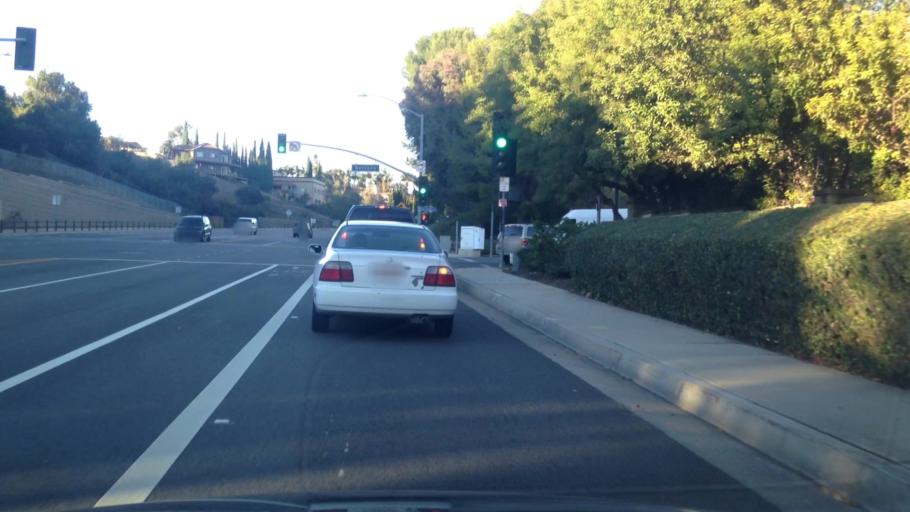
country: US
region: California
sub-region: Orange County
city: Villa Park
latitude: 33.8199
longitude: -117.7958
